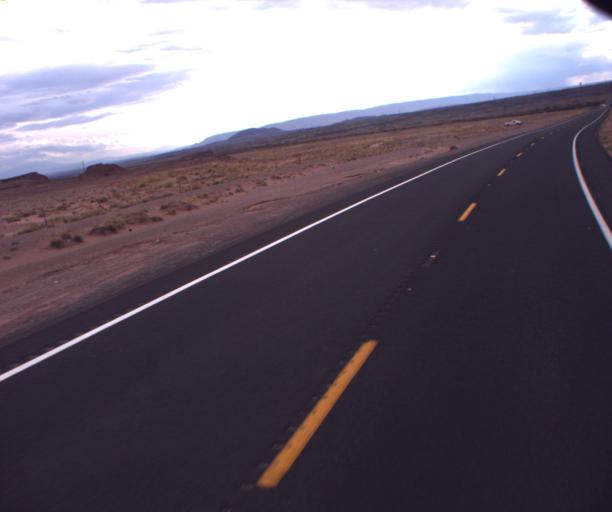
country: US
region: Arizona
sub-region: Coconino County
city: Tuba City
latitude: 36.0818
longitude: -111.3702
